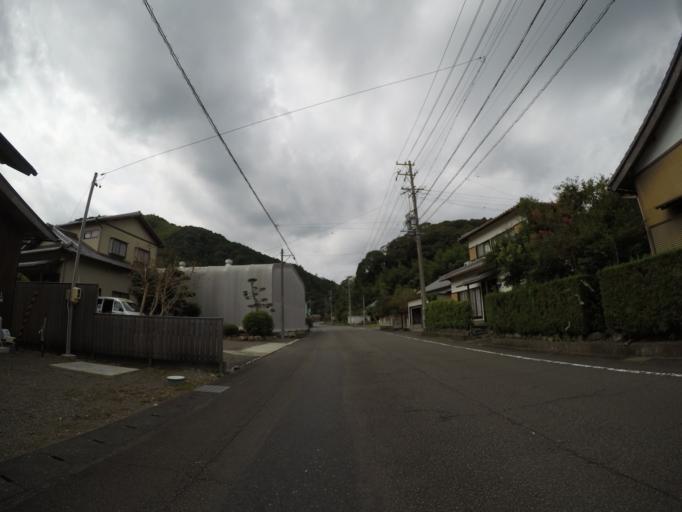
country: JP
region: Shizuoka
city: Fujieda
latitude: 34.9044
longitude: 138.1971
